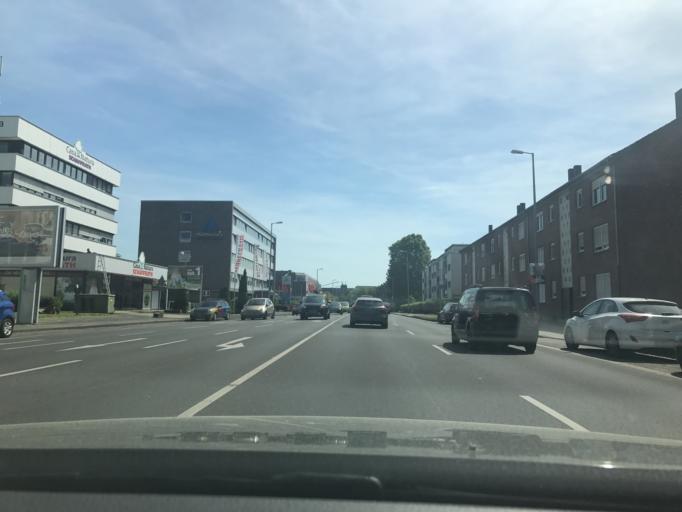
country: DE
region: North Rhine-Westphalia
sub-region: Regierungsbezirk Dusseldorf
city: Monchengladbach
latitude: 51.1844
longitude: 6.4439
